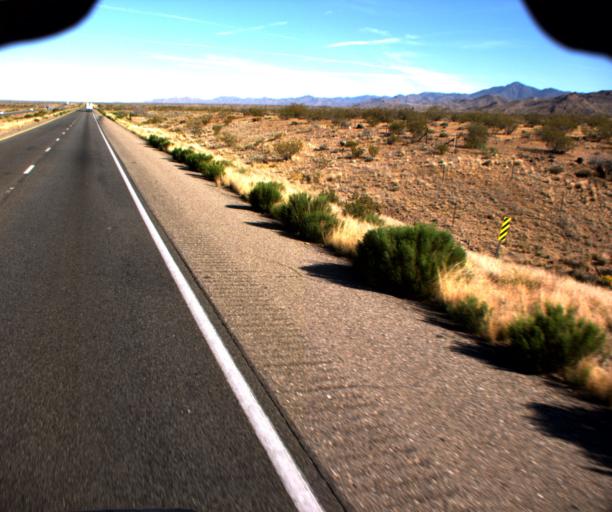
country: US
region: Arizona
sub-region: Mohave County
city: Golden Valley
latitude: 35.2602
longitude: -114.1601
